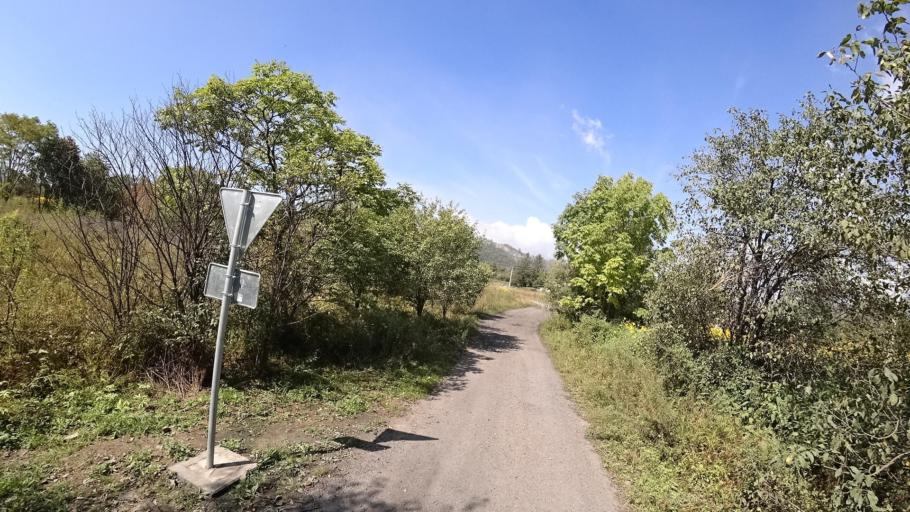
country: RU
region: Jewish Autonomous Oblast
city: Londoko
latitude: 49.0041
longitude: 131.9440
